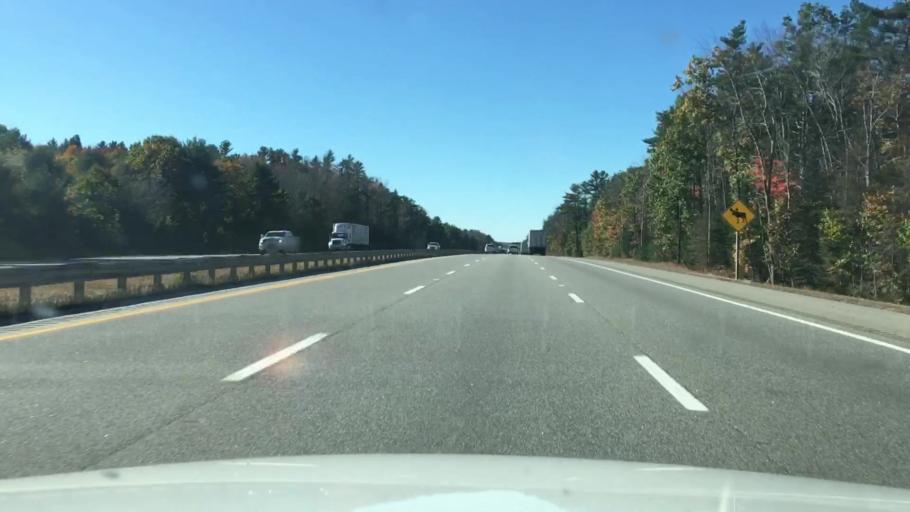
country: US
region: Maine
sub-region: York County
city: West Kennebunk
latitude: 43.4541
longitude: -70.5298
